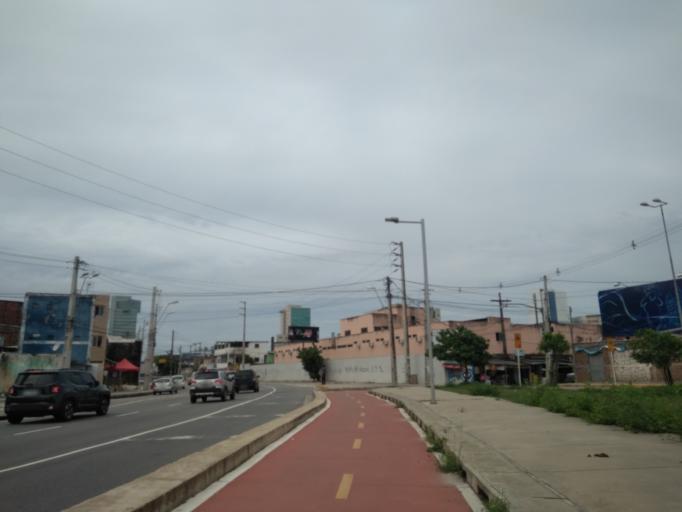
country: BR
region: Pernambuco
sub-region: Recife
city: Recife
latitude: -8.0884
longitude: -34.8901
